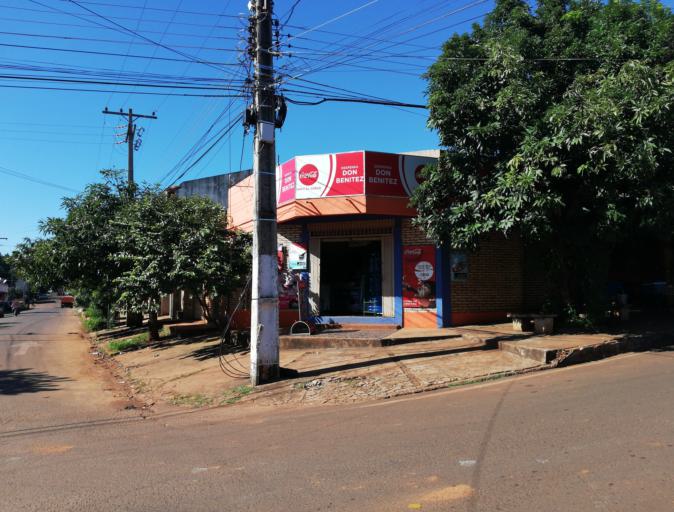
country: PY
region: Alto Parana
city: Ciudad del Este
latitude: -25.5034
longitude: -54.6437
